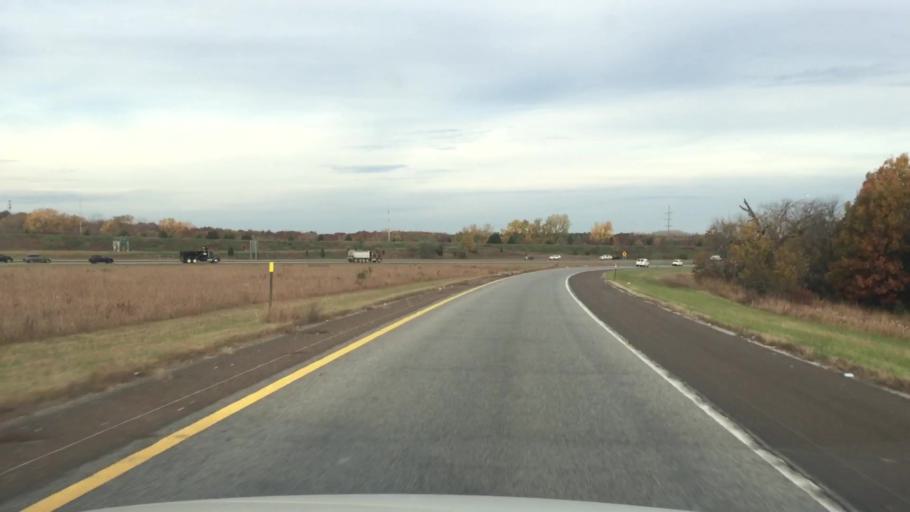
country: US
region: Kansas
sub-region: Wyandotte County
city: Edwardsville
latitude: 39.0123
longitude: -94.7828
